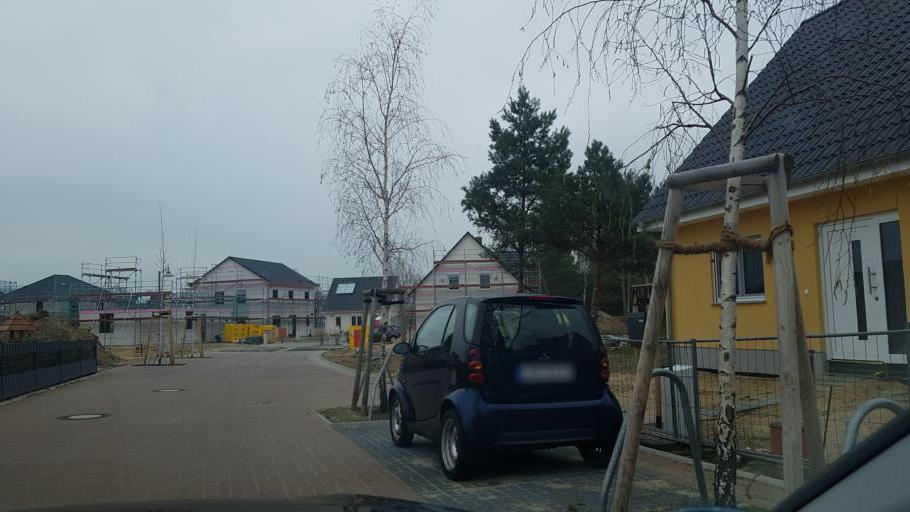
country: DE
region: Brandenburg
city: Mittenwalde
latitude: 52.2897
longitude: 13.5373
